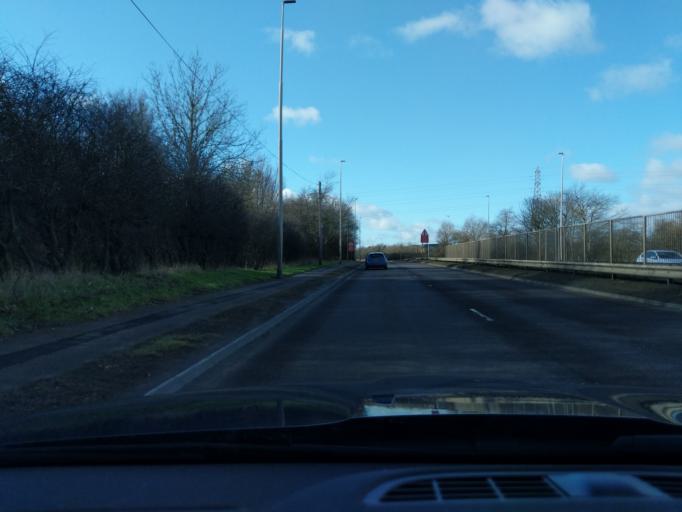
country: GB
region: England
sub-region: South Tyneside
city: Hebburn
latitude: 54.9550
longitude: -1.4990
